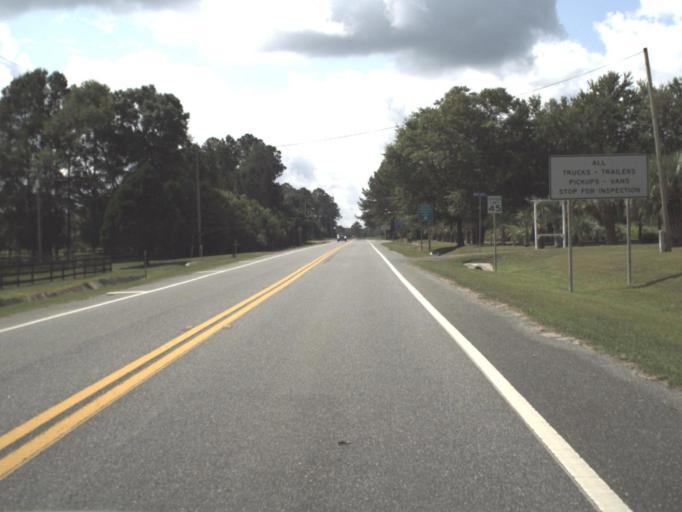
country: US
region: Florida
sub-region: Baker County
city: Macclenny
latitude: 30.3614
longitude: -82.1339
